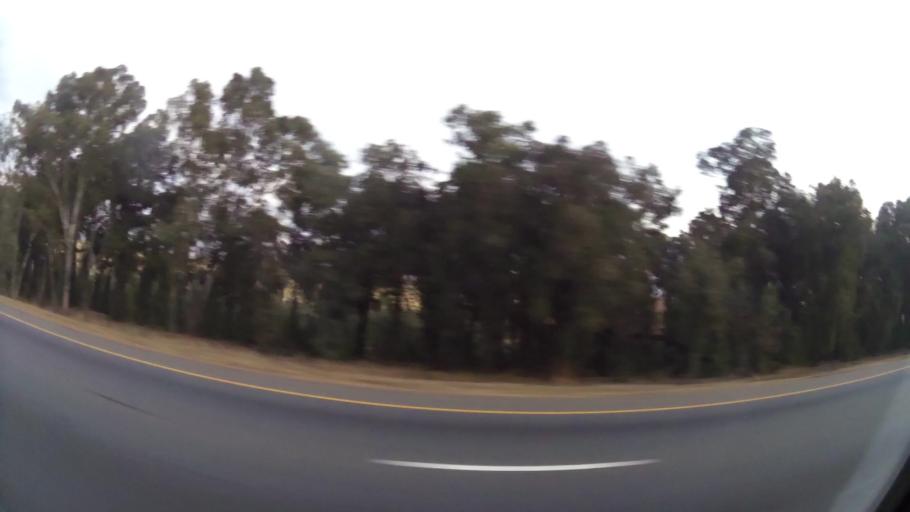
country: ZA
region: Gauteng
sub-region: Ekurhuleni Metropolitan Municipality
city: Germiston
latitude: -26.2516
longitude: 28.2223
